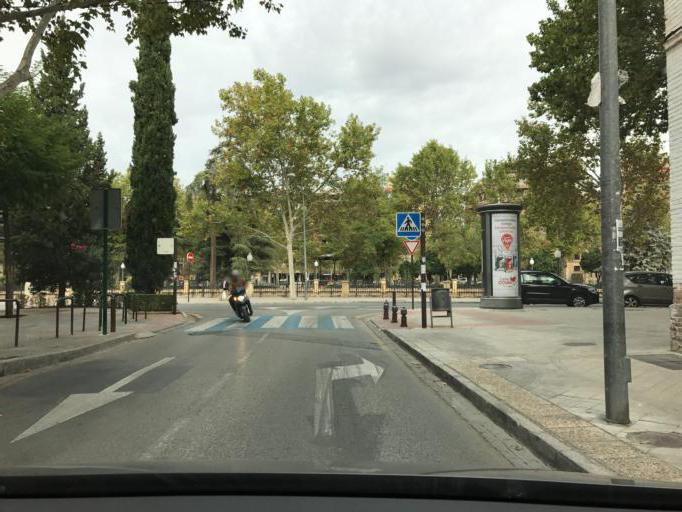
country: ES
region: Andalusia
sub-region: Provincia de Granada
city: Granada
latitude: 37.1686
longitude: -3.5940
